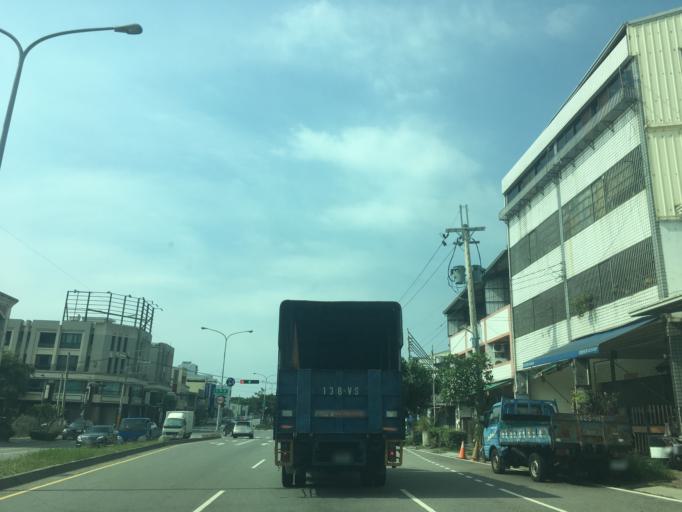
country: TW
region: Taiwan
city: Fengyuan
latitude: 24.2502
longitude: 120.7374
